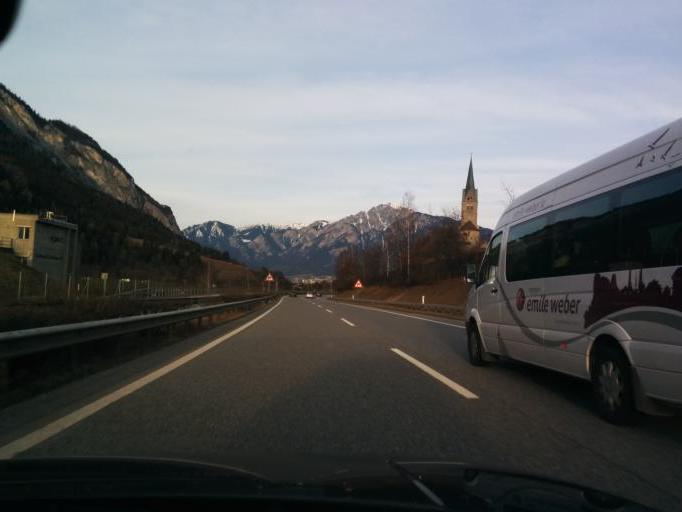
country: CH
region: Grisons
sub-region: Imboden District
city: Domat
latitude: 46.8369
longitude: 9.4465
